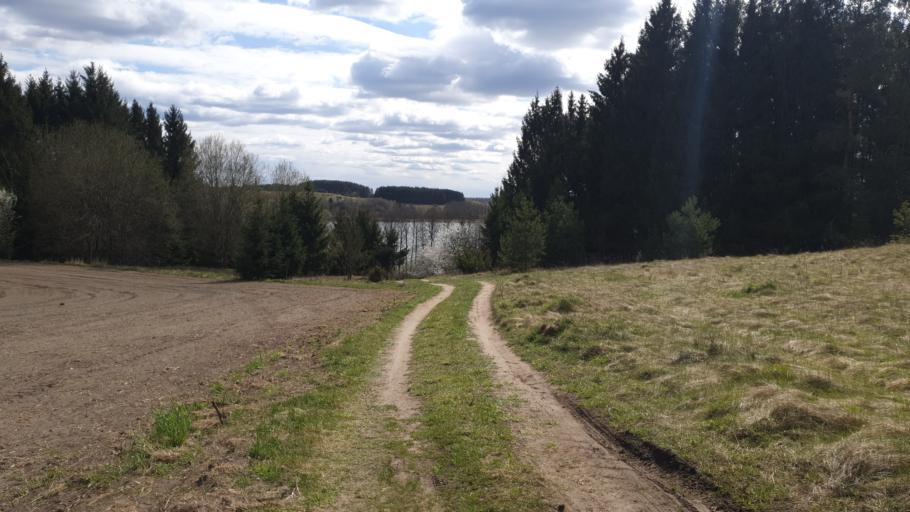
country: LT
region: Vilnius County
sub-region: Trakai
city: Rudiskes
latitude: 54.5098
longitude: 24.6834
